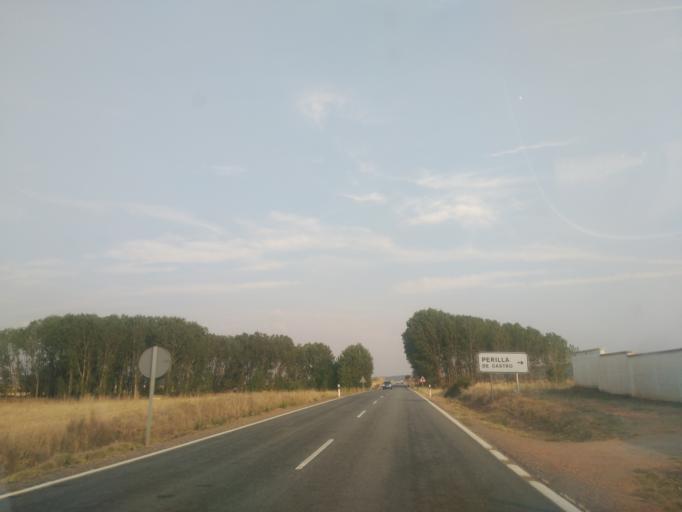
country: ES
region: Castille and Leon
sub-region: Provincia de Zamora
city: Pozuelo de Tabara
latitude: 41.7810
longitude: -5.8896
